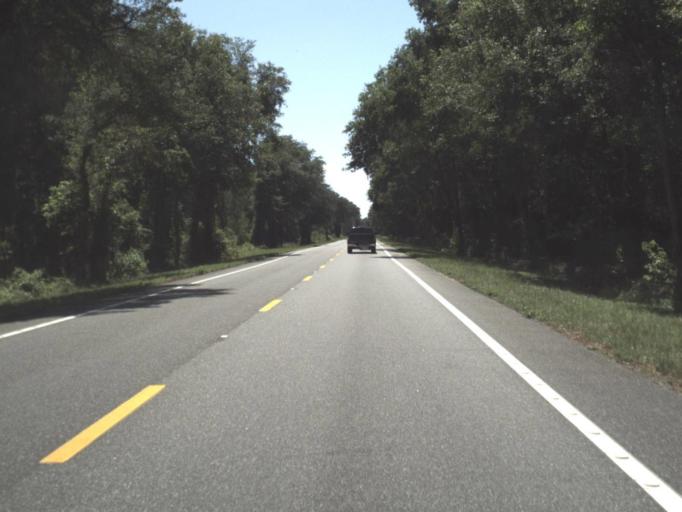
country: US
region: Florida
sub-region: Lafayette County
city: Mayo
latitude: 30.1294
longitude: -83.3313
